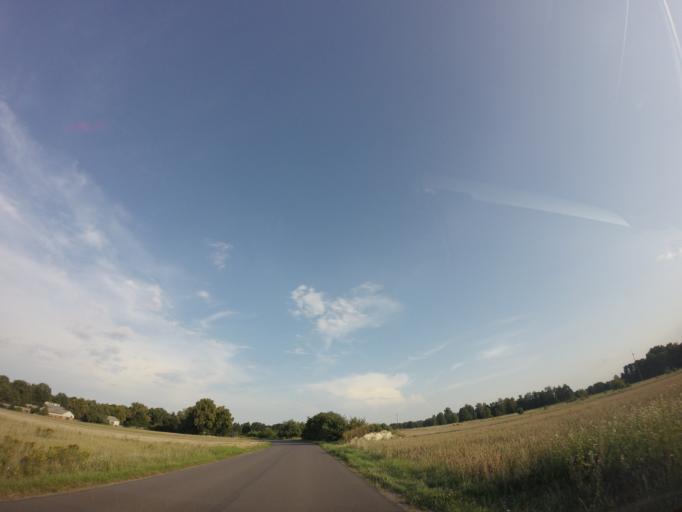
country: PL
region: Lublin Voivodeship
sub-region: Powiat pulawski
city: Kurow
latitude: 51.4272
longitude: 22.2184
